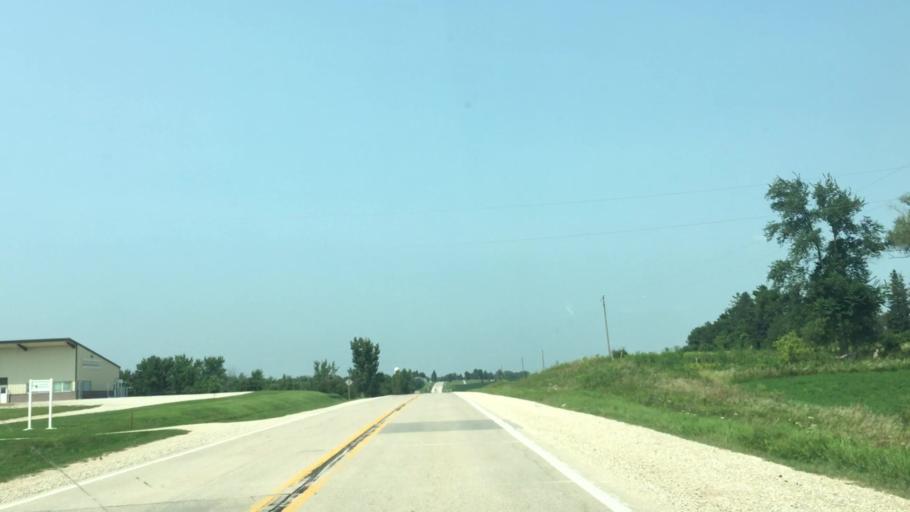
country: US
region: Iowa
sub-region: Winneshiek County
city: Decorah
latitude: 43.1649
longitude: -91.8644
